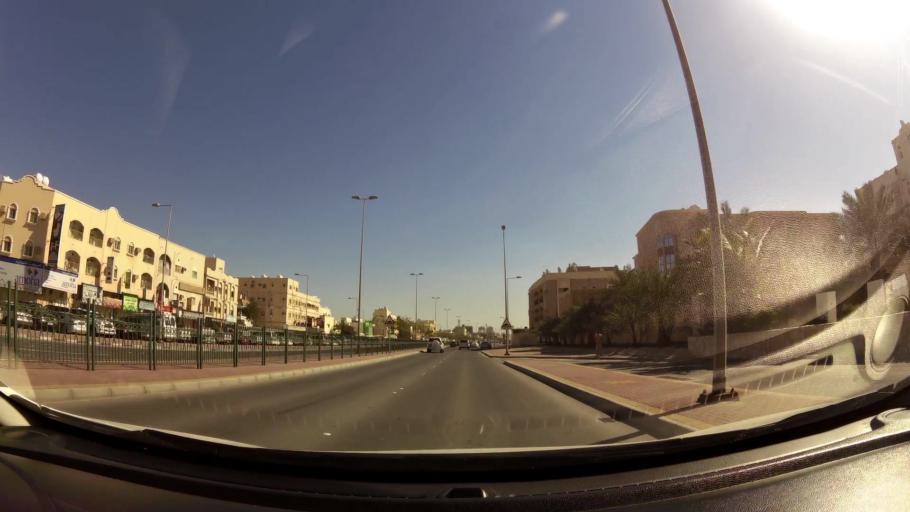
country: BH
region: Muharraq
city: Al Hadd
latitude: 26.2415
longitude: 50.6517
